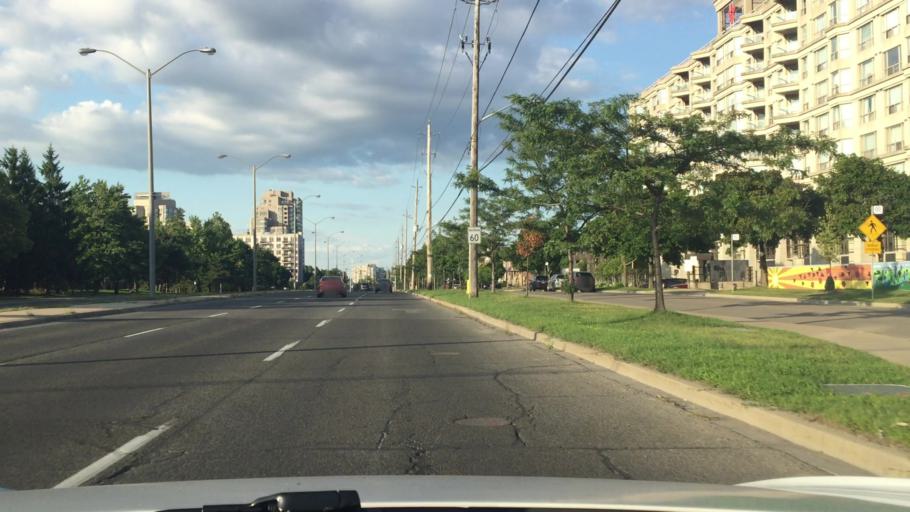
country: CA
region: Ontario
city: Scarborough
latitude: 43.7391
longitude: -79.2166
